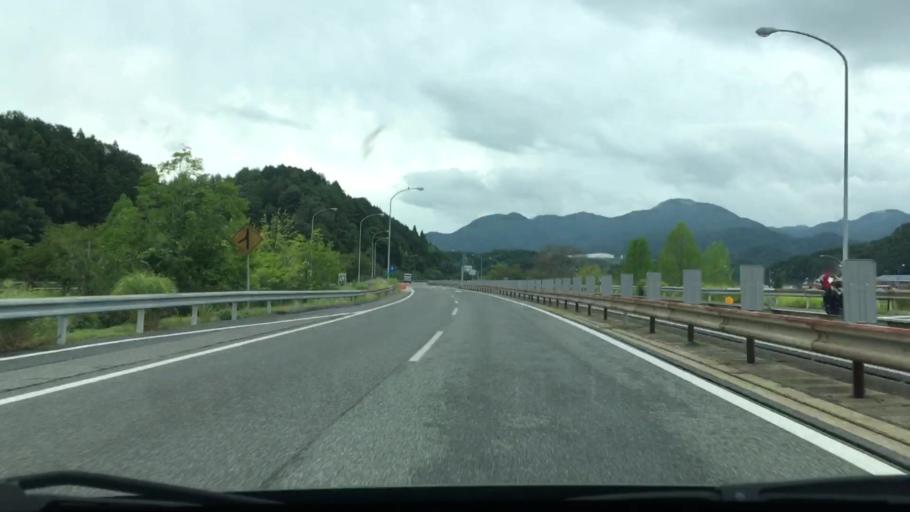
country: JP
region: Hiroshima
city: Hiroshima-shi
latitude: 34.6726
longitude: 132.5437
